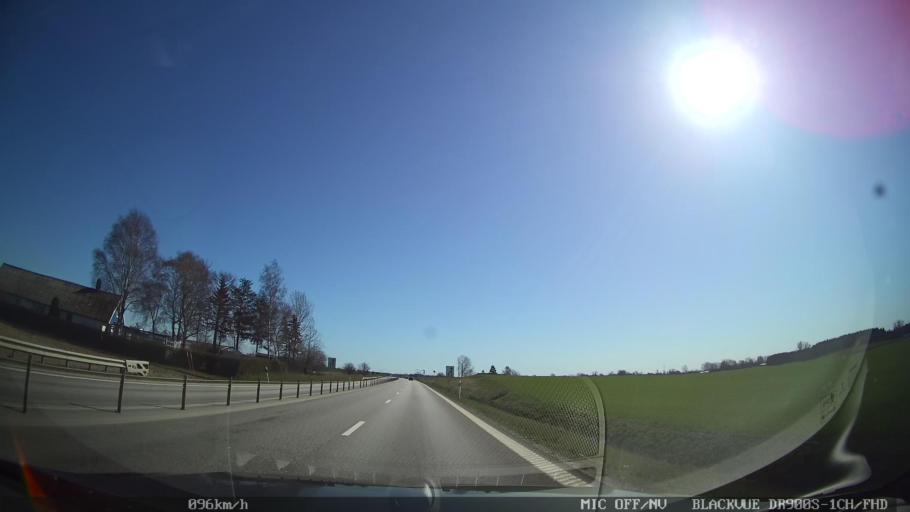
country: SE
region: Skane
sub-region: Skurups Kommun
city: Skurup
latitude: 55.4898
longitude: 13.5449
